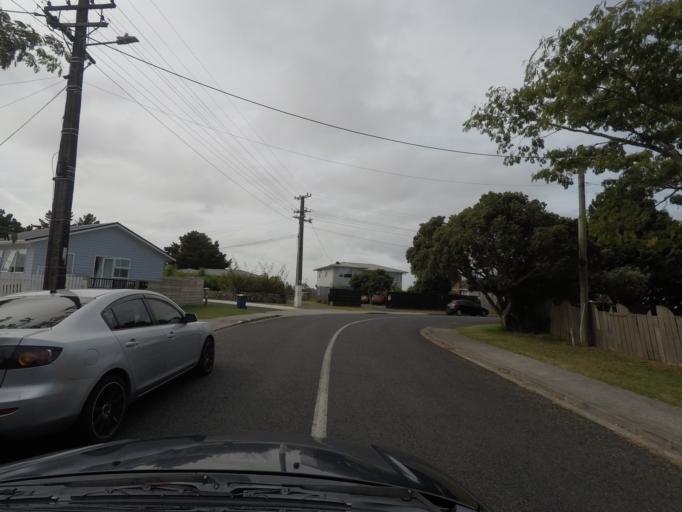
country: NZ
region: Auckland
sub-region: Auckland
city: Rosebank
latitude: -36.8906
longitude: 174.6669
